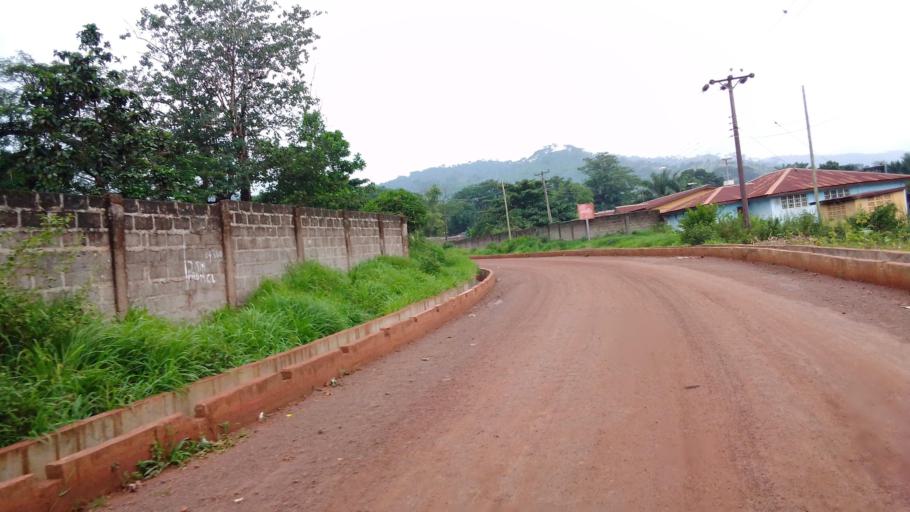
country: SL
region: Eastern Province
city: Kenema
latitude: 7.8857
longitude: -11.1909
